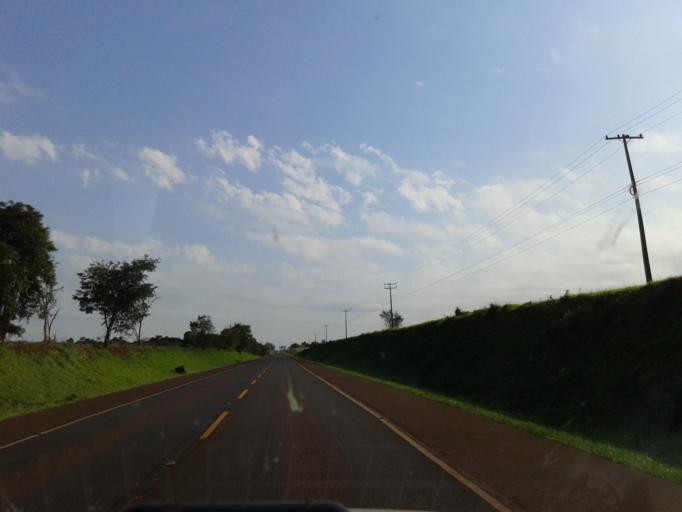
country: PY
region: Itapua
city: Edelira
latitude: -26.7570
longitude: -55.3738
